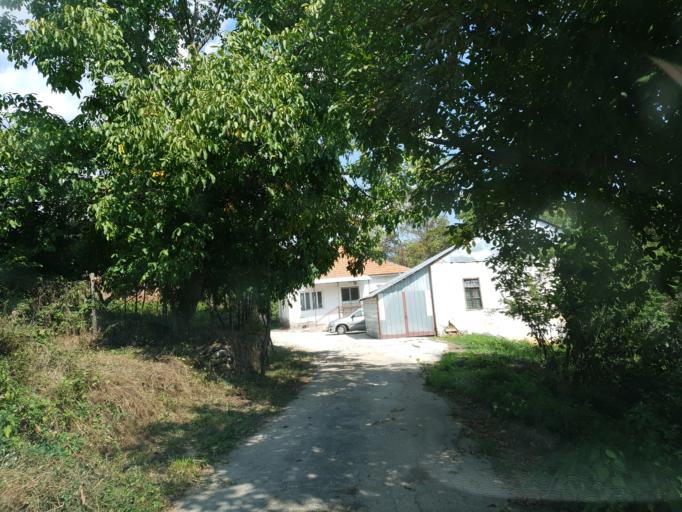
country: MK
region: Makedonski Brod
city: Samokov
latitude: 41.7459
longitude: 21.1045
